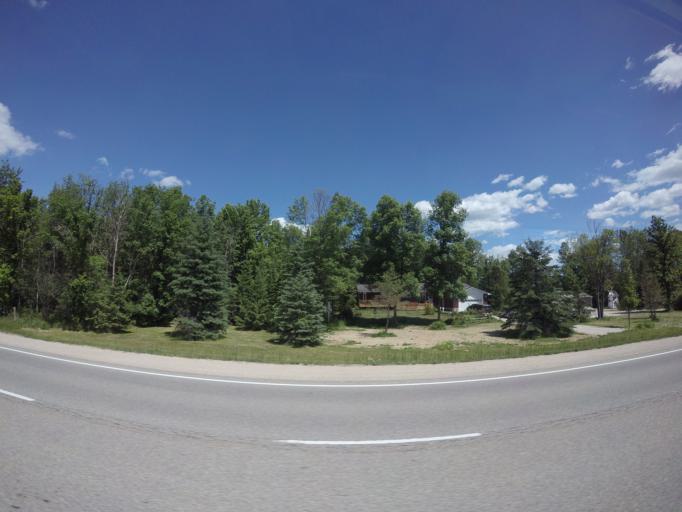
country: CA
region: Ontario
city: Perth
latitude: 44.9850
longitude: -76.2271
